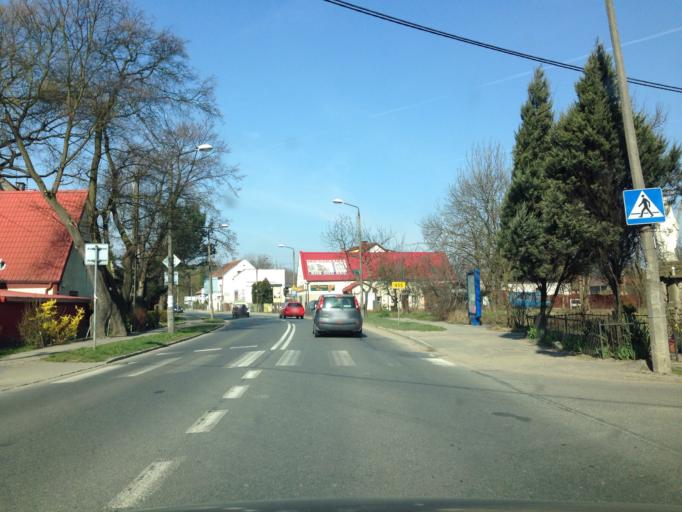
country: PL
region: Lower Silesian Voivodeship
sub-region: Powiat wroclawski
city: Wilczyce
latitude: 51.1143
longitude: 17.1304
